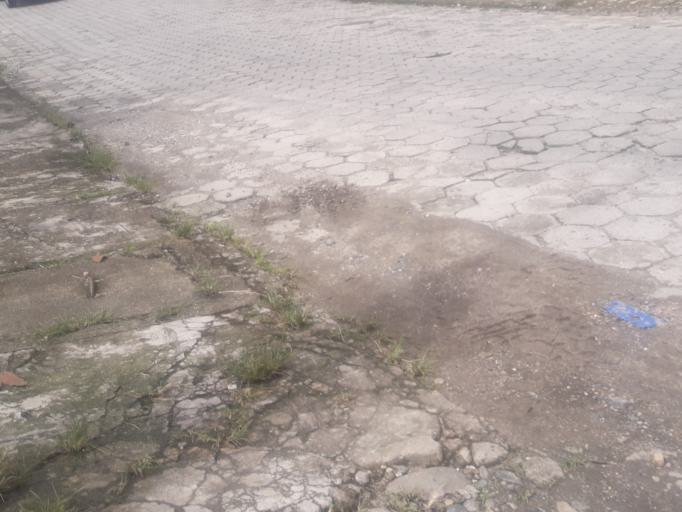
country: EC
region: Napo
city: Tena
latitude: -0.9977
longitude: -77.8114
